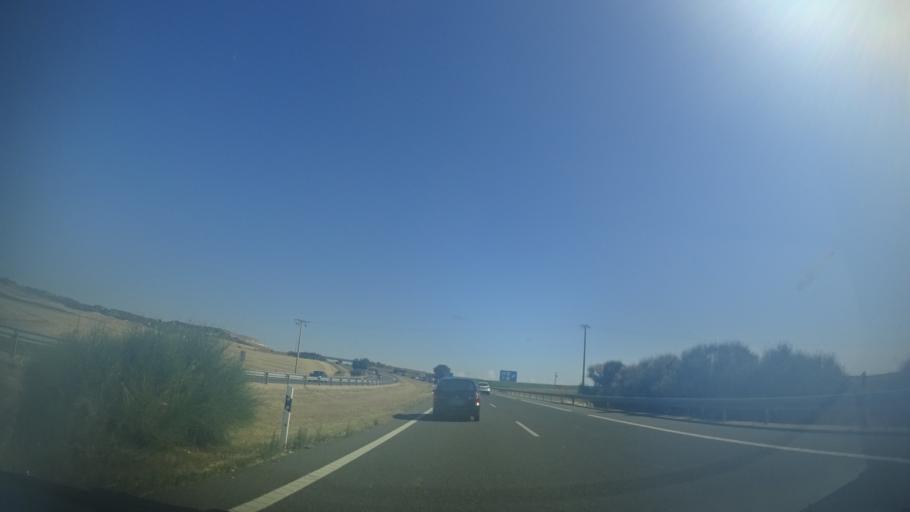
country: ES
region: Castille and Leon
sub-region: Provincia de Valladolid
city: Vega de Valdetronco
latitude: 41.5861
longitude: -5.1117
